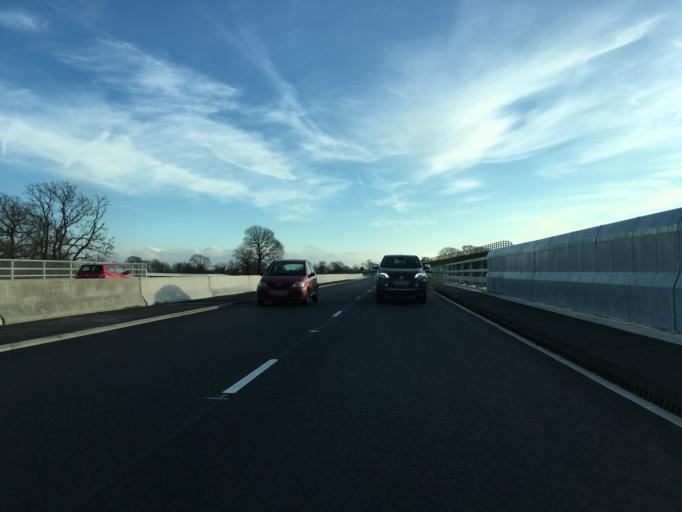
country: GB
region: England
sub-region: Cheshire East
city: Wilmslow
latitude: 53.3600
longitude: -2.2398
